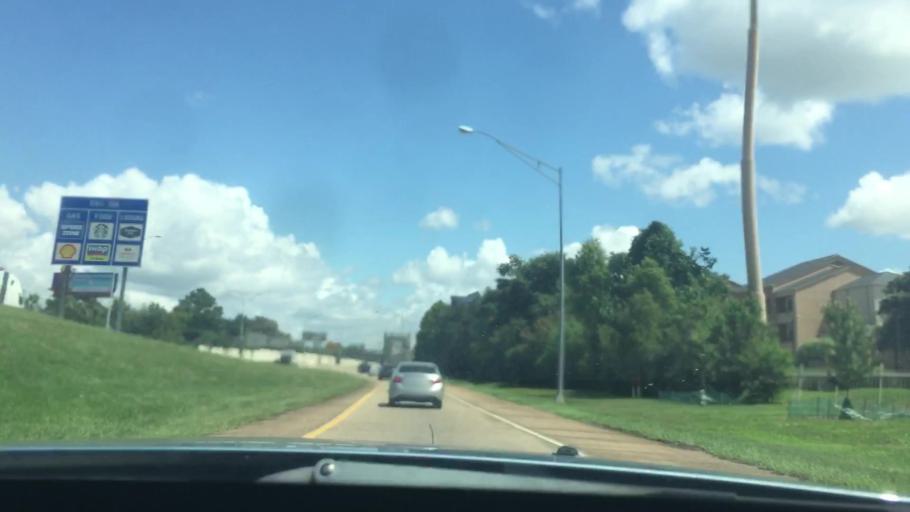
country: US
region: Louisiana
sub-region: East Baton Rouge Parish
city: Baton Rouge
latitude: 30.4232
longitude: -91.1515
